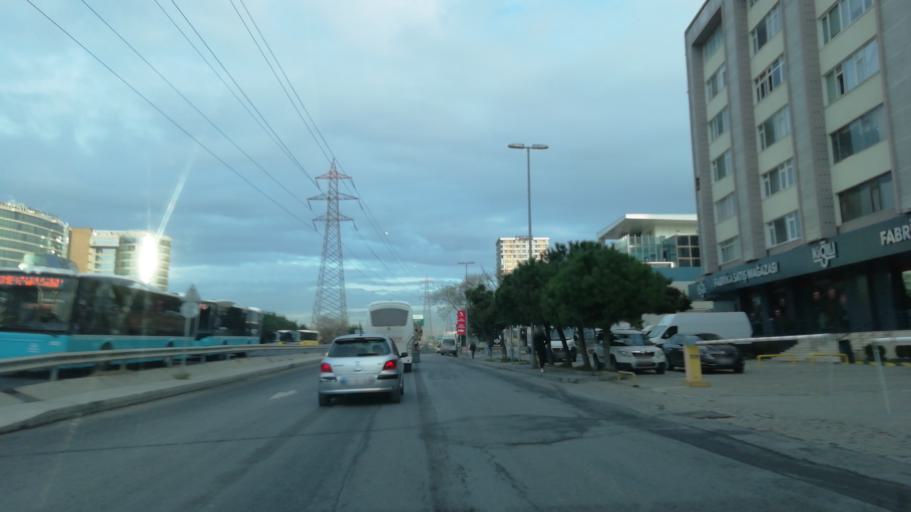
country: TR
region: Istanbul
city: Bahcelievler
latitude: 41.0041
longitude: 28.8151
